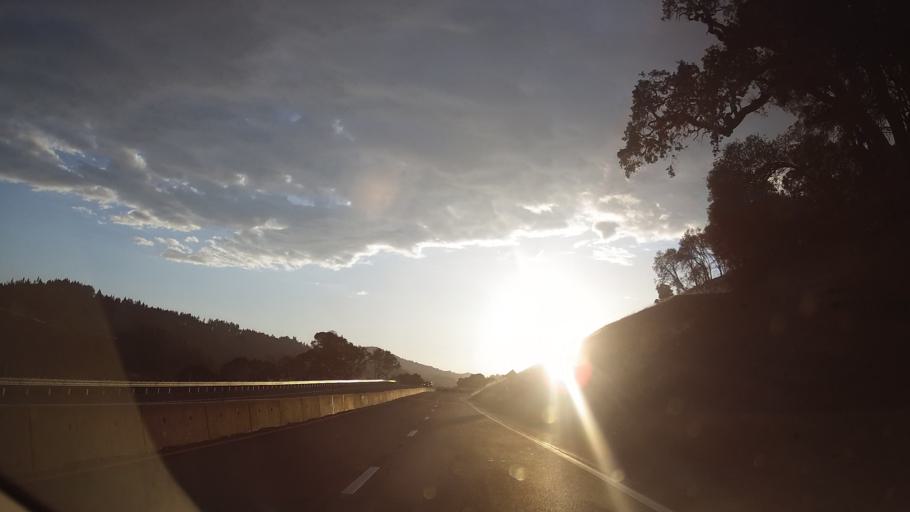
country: US
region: California
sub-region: Mendocino County
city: Redwood Valley
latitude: 39.2967
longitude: -123.2804
